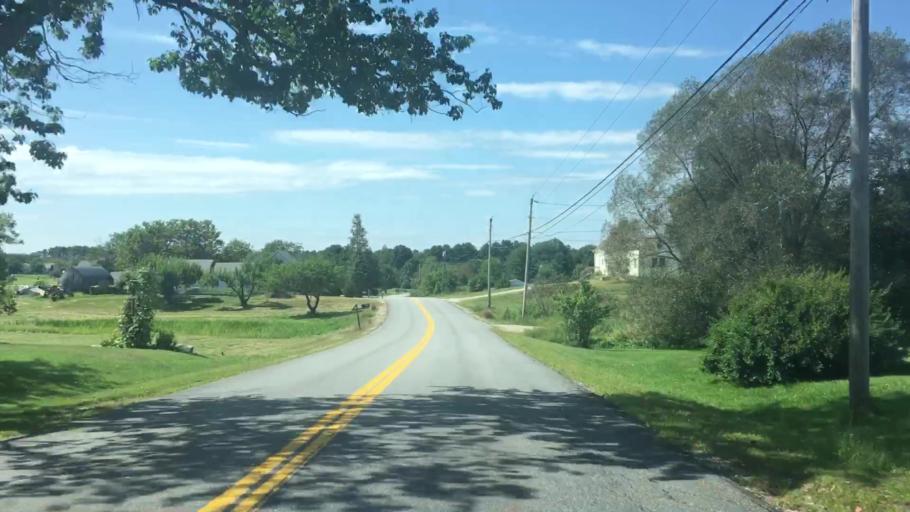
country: US
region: Maine
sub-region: Androscoggin County
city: Lisbon
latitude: 44.0533
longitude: -70.1069
